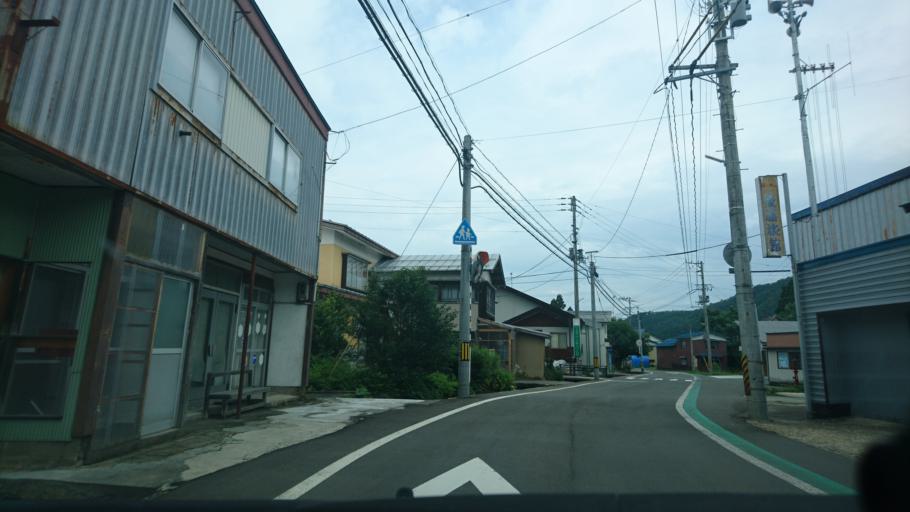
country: JP
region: Akita
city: Yuzawa
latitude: 39.1805
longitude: 140.6456
